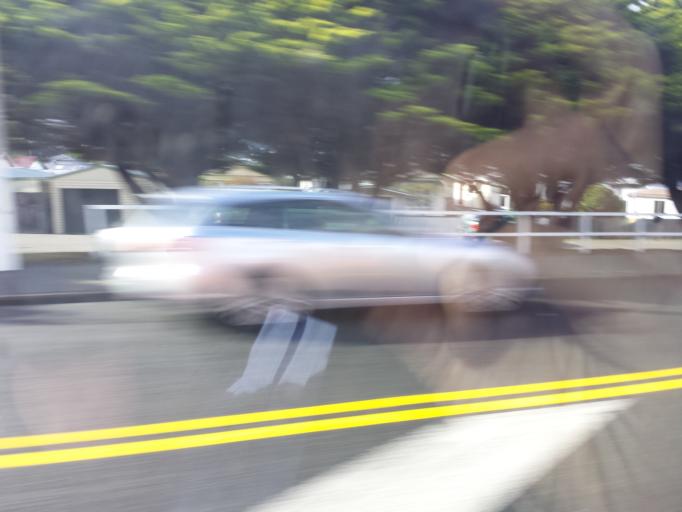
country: NZ
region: Wellington
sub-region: Wellington City
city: Wellington
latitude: -41.3212
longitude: 174.8091
